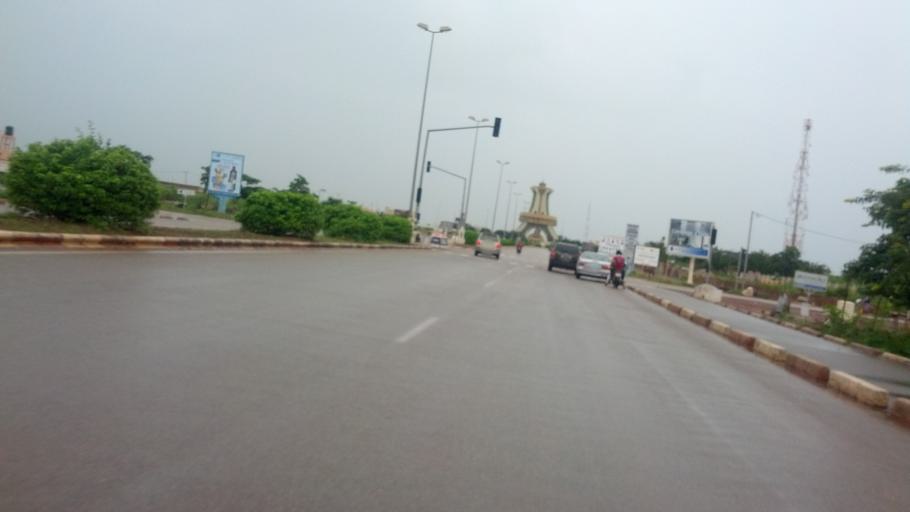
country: BF
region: Centre
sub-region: Kadiogo Province
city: Ouagadougou
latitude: 12.3184
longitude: -1.5027
